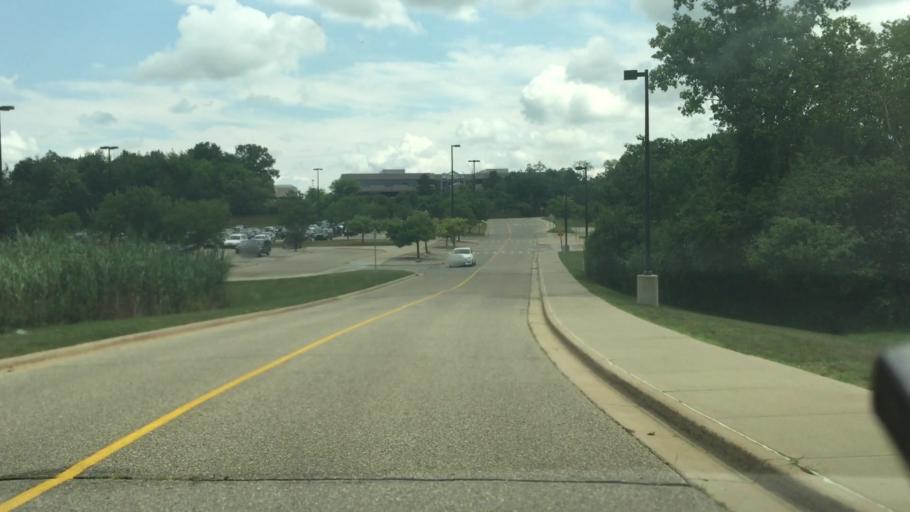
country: US
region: Michigan
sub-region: Oakland County
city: Auburn Hills
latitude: 42.6483
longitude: -83.2256
